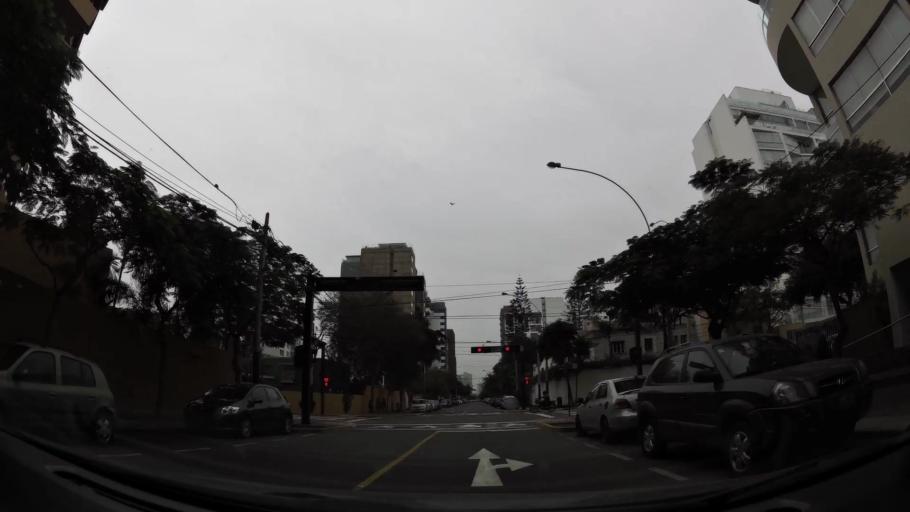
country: PE
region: Lima
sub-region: Lima
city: San Isidro
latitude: -12.0961
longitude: -77.0448
